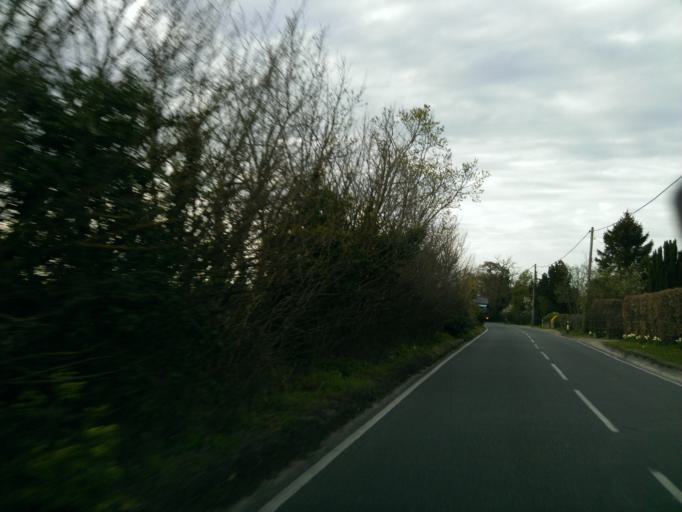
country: GB
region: England
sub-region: Essex
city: Wivenhoe
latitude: 51.8565
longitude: 0.9766
